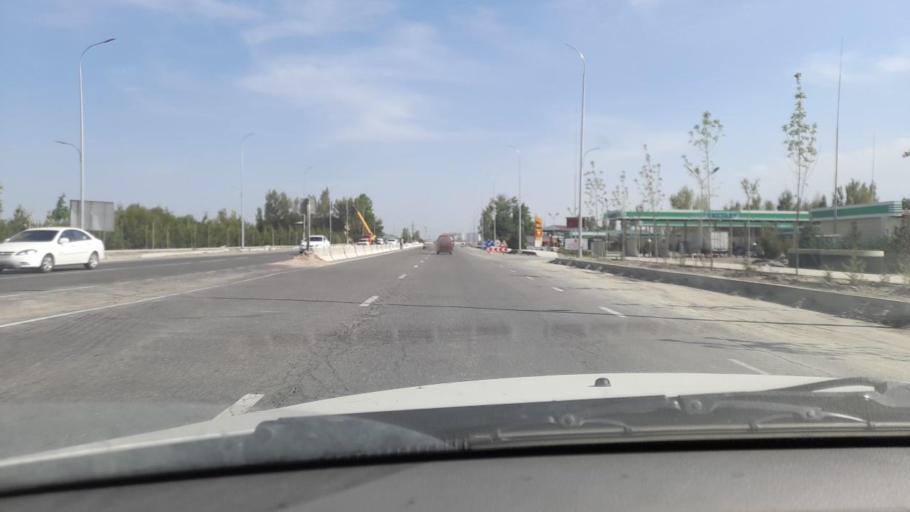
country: UZ
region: Samarqand
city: Daxbet
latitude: 39.7469
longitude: 66.9230
